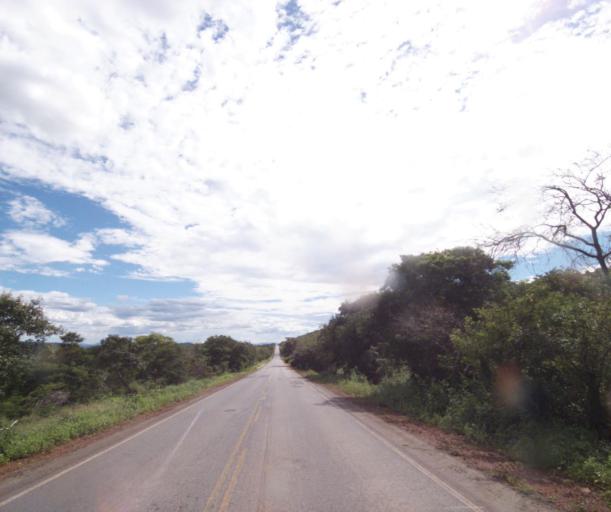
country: BR
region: Minas Gerais
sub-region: Espinosa
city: Espinosa
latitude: -14.7848
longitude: -42.6859
